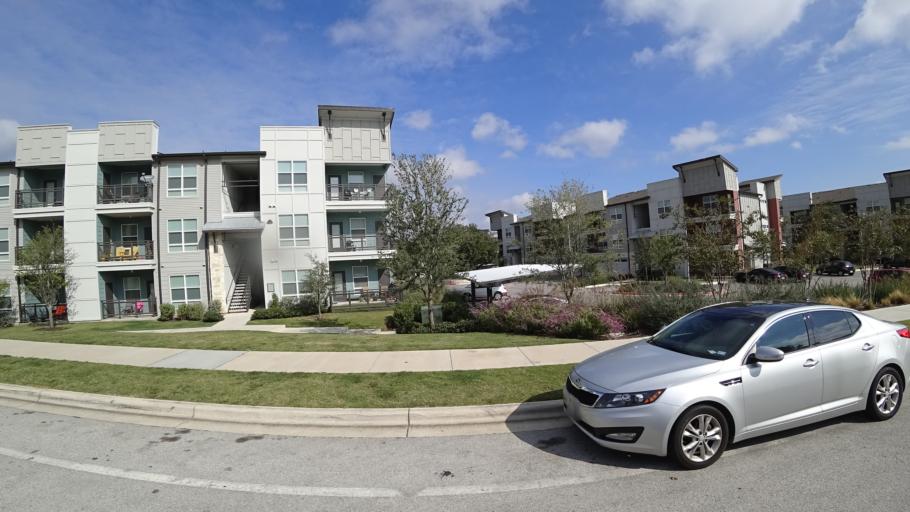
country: US
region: Texas
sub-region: Williamson County
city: Jollyville
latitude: 30.4374
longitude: -97.7319
